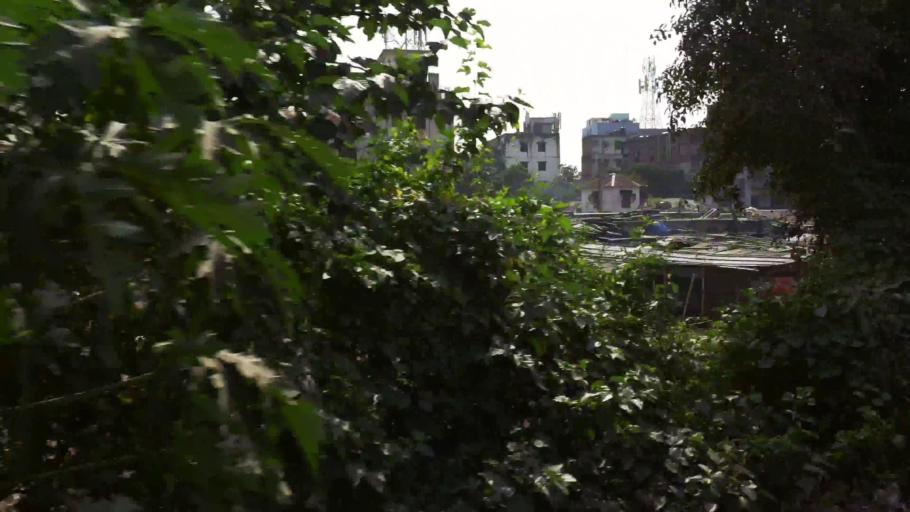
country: BD
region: Dhaka
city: Tungi
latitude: 23.8750
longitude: 90.4059
